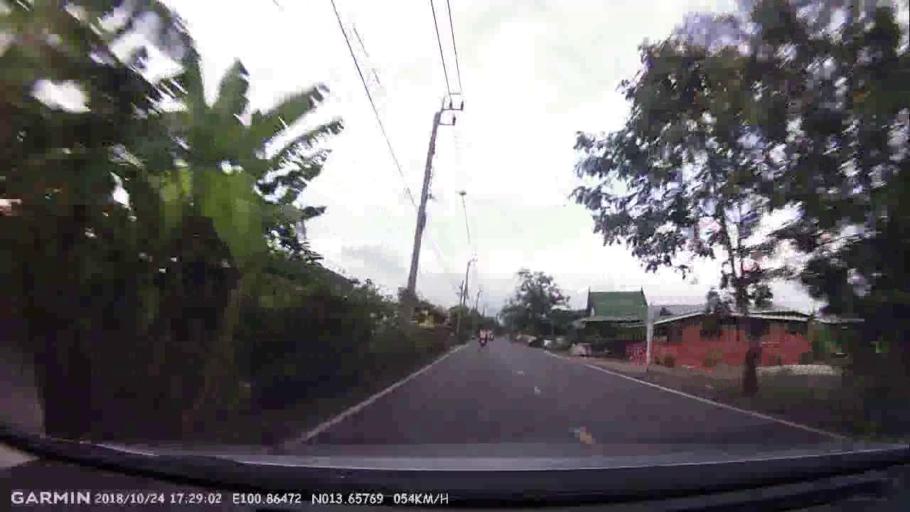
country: TH
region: Samut Prakan
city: Ban Khlong Bang Sao Thong
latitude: 13.6578
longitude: 100.8647
